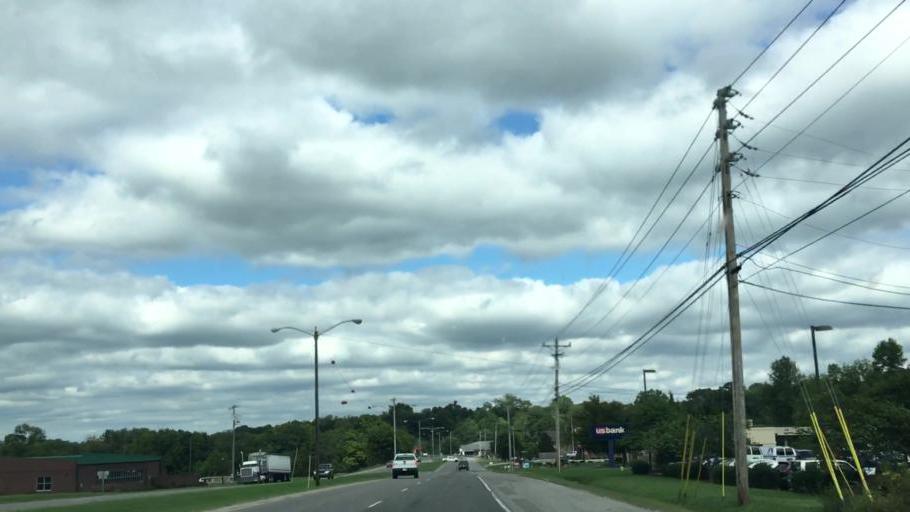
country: US
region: Tennessee
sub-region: Maury County
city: Columbia
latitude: 35.6125
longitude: -87.0678
